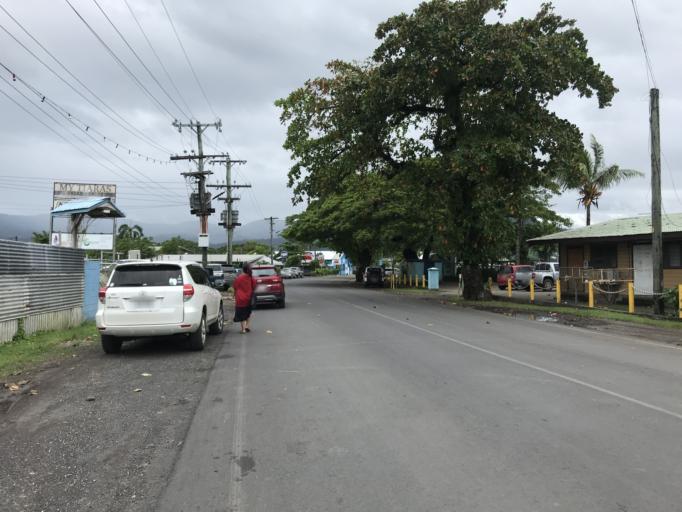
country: WS
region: Tuamasaga
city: Apia
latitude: -13.8274
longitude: -171.7587
